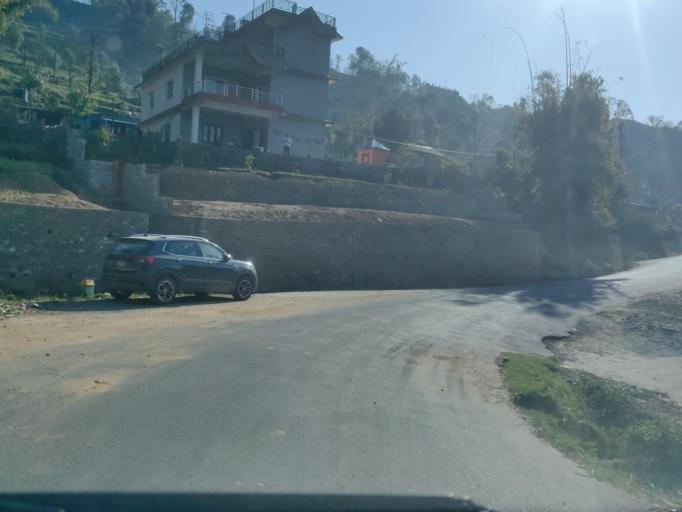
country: NP
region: Western Region
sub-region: Gandaki Zone
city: Pokhara
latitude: 28.2370
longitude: 83.9647
